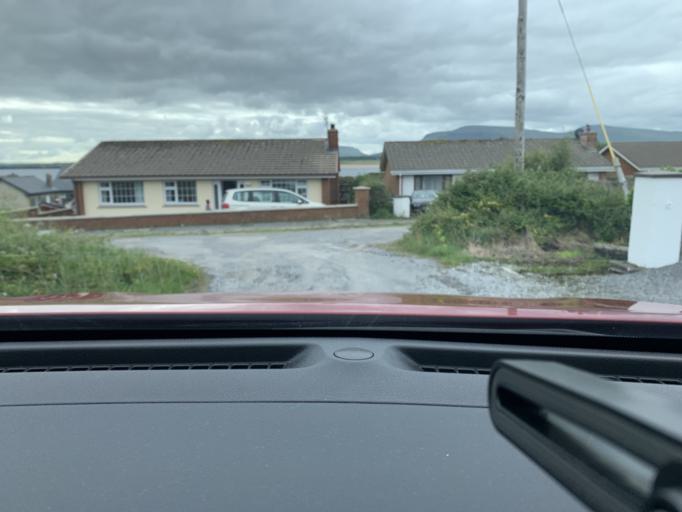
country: IE
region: Ulster
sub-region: County Donegal
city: Killybegs
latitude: 54.4652
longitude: -8.4513
